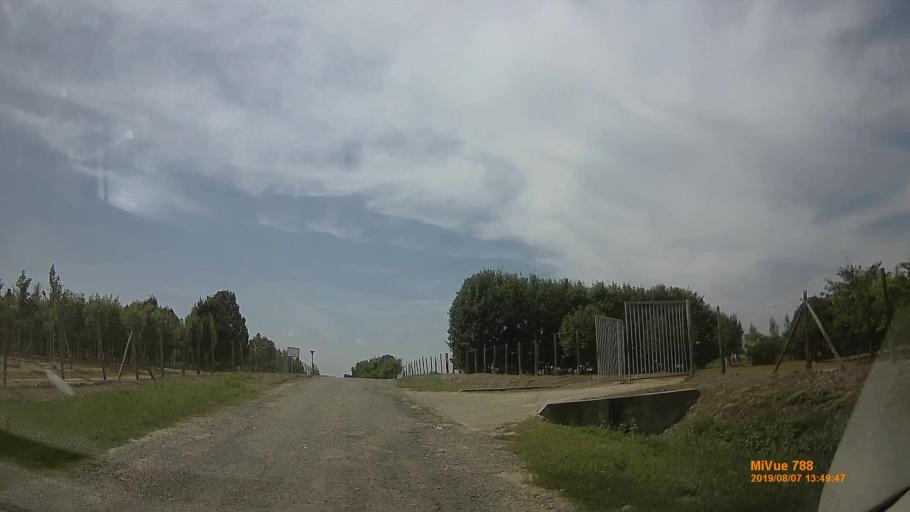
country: HU
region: Zala
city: Cserszegtomaj
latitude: 46.8888
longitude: 17.1893
